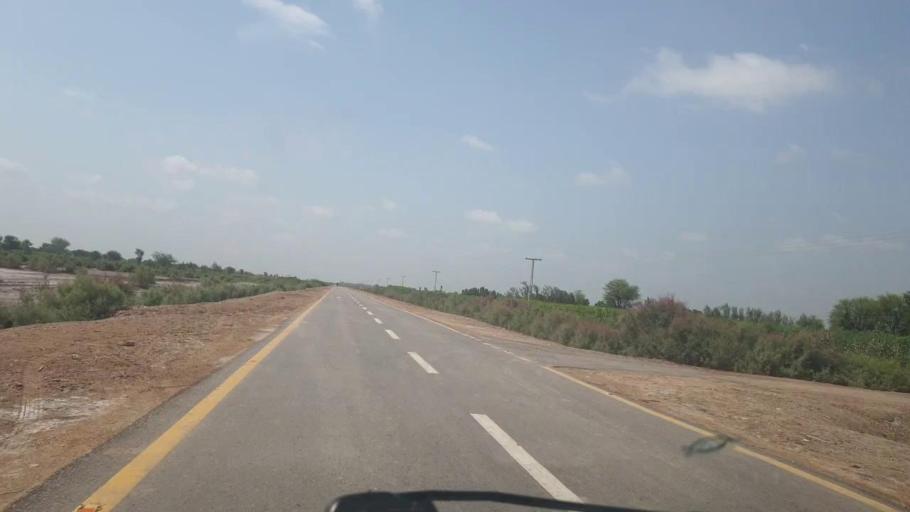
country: PK
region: Sindh
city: Berani
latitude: 25.7312
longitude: 68.9443
